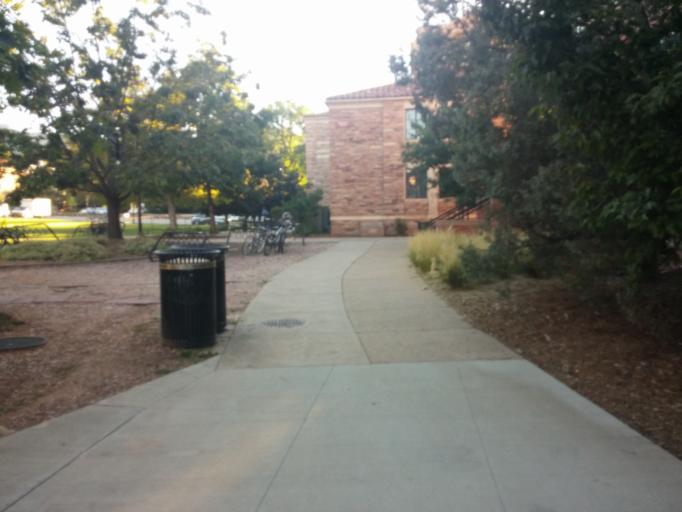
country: US
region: Colorado
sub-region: Boulder County
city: Boulder
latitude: 40.0103
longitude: -105.2704
